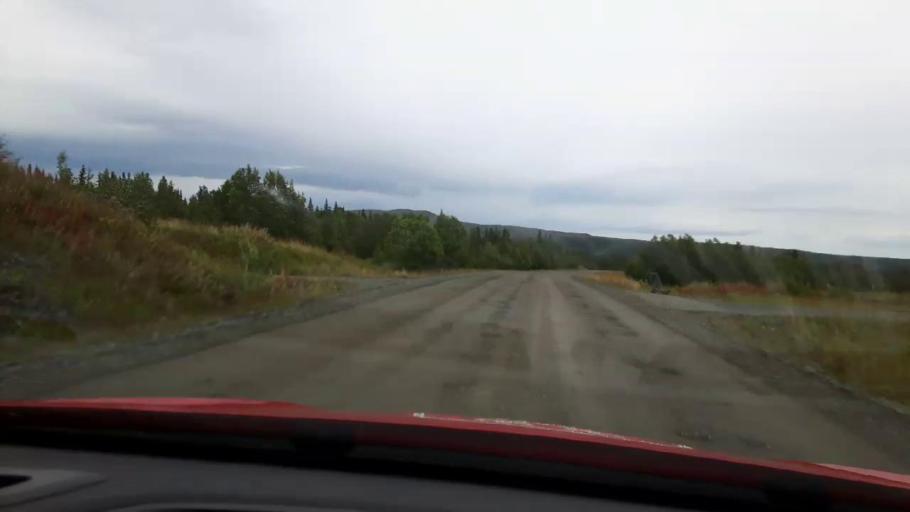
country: NO
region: Nord-Trondelag
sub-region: Meraker
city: Meraker
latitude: 63.5597
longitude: 12.3454
